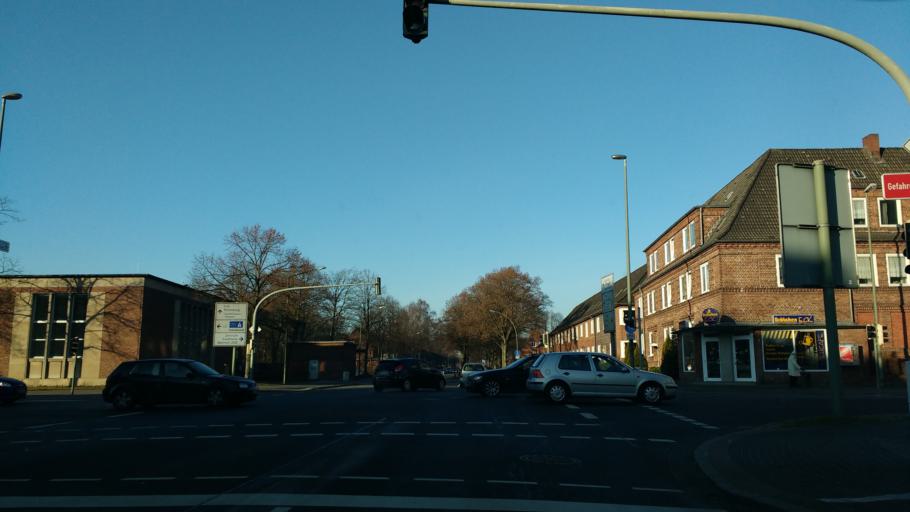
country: DE
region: Schleswig-Holstein
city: Neumunster
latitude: 54.0742
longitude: 9.9687
